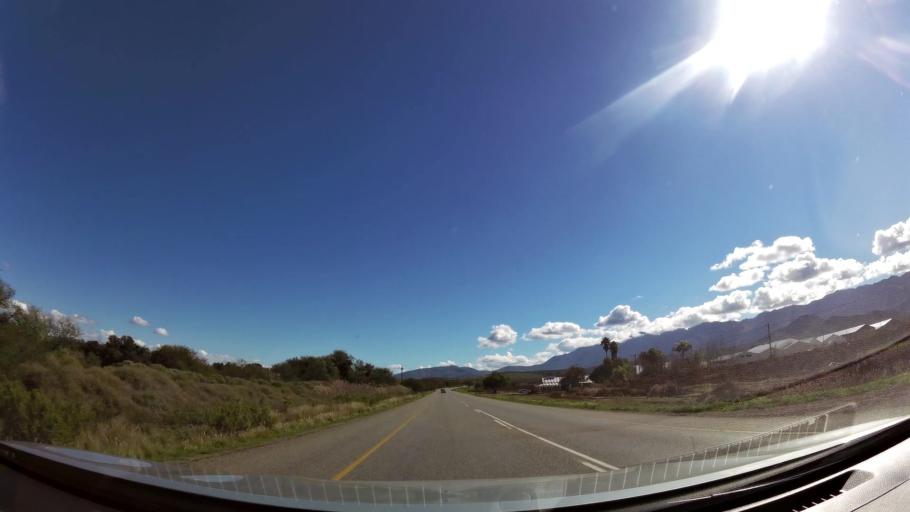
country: ZA
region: Western Cape
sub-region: Cape Winelands District Municipality
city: Ashton
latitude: -33.8267
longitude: 19.9846
